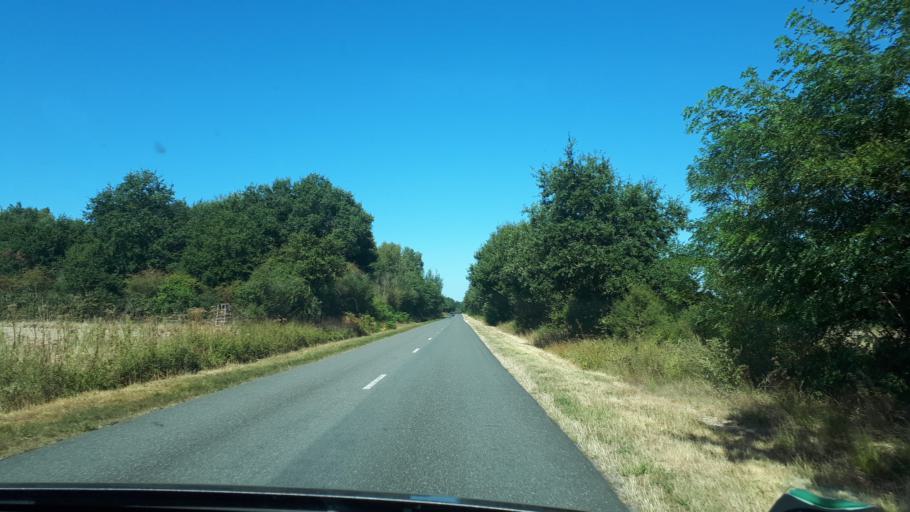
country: FR
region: Centre
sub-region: Departement du Loiret
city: Cerdon
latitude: 47.6386
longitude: 2.4129
